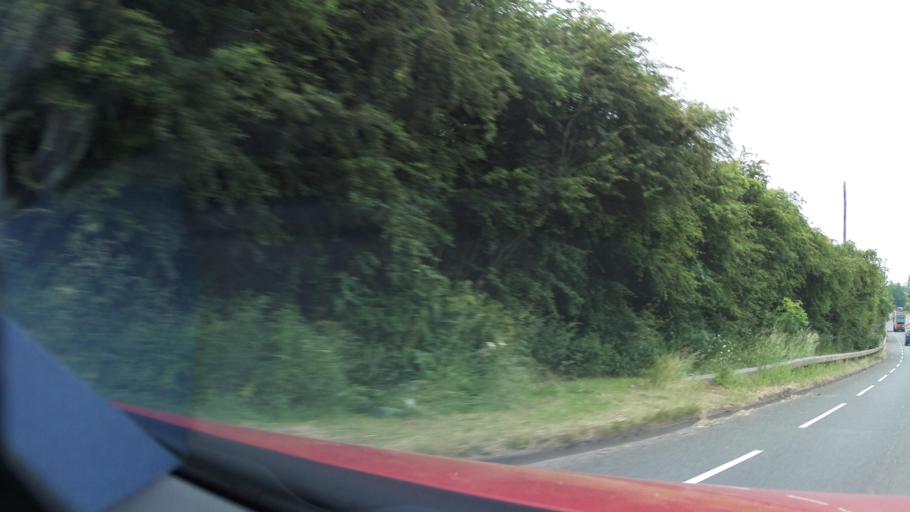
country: GB
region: England
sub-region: Derbyshire
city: Swadlincote
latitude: 52.7690
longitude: -1.5936
